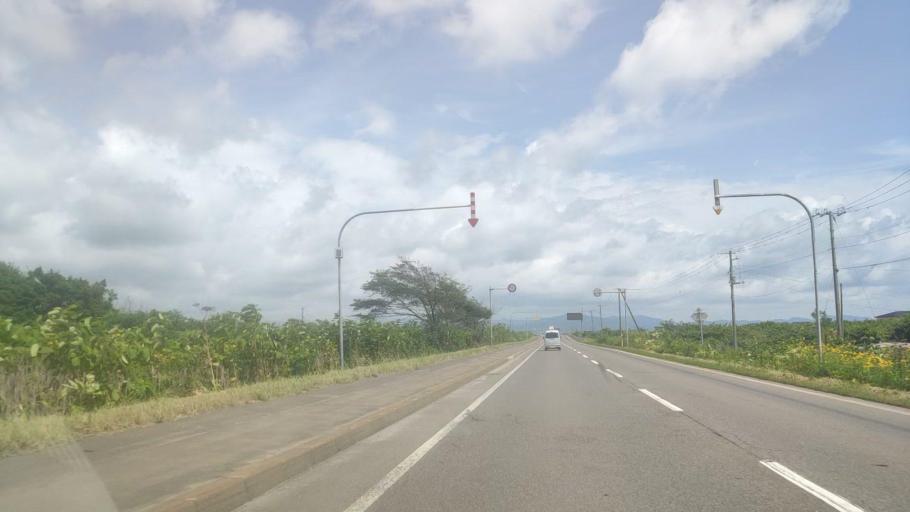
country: JP
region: Hokkaido
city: Niseko Town
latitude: 42.5218
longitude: 140.3847
